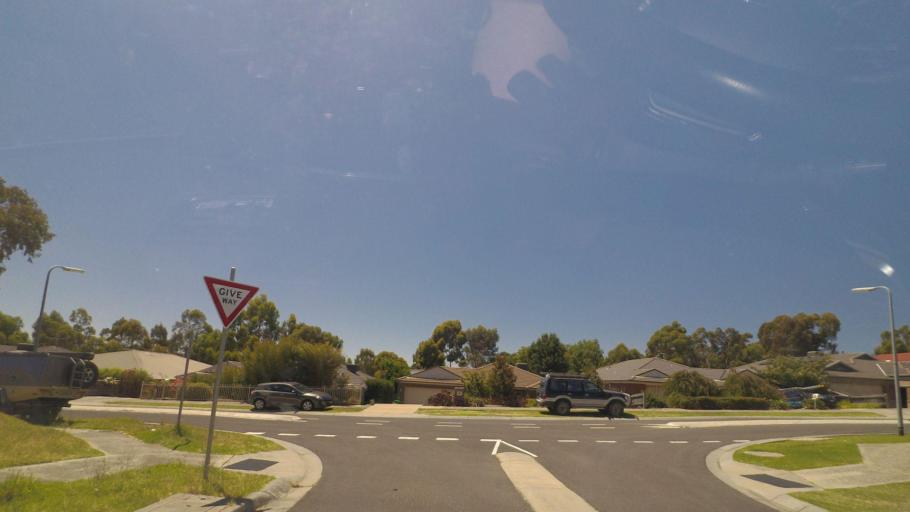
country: AU
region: Victoria
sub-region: Yarra Ranges
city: Lilydale
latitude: -37.7390
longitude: 145.3426
